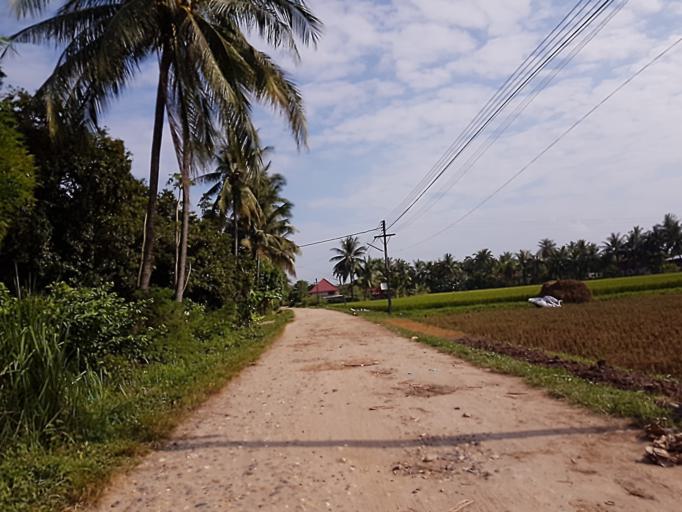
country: TH
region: Nong Khai
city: Tha Bo
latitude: 17.8673
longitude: 102.6067
